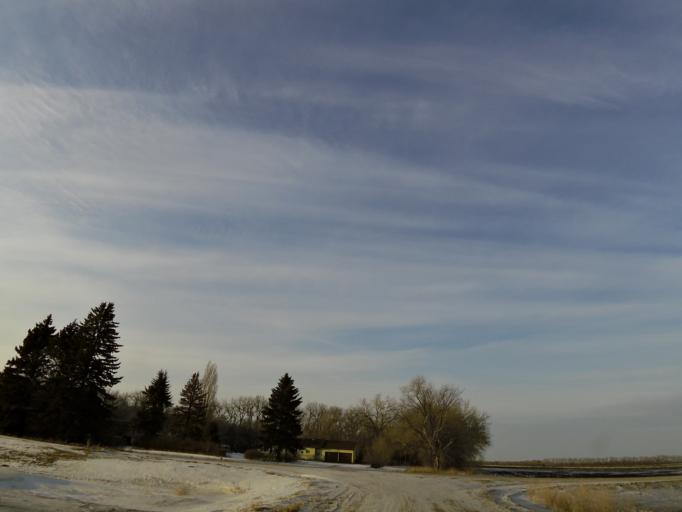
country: US
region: North Dakota
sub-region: Walsh County
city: Grafton
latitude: 48.5135
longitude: -97.4418
